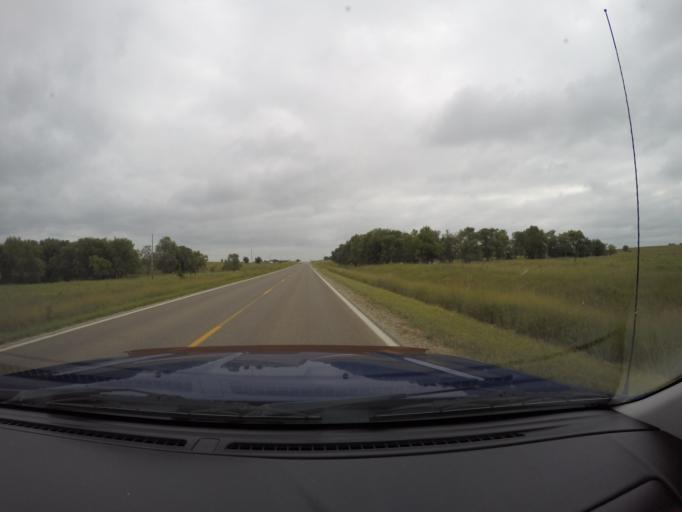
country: US
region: Kansas
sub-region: Morris County
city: Council Grove
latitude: 38.8465
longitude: -96.5015
